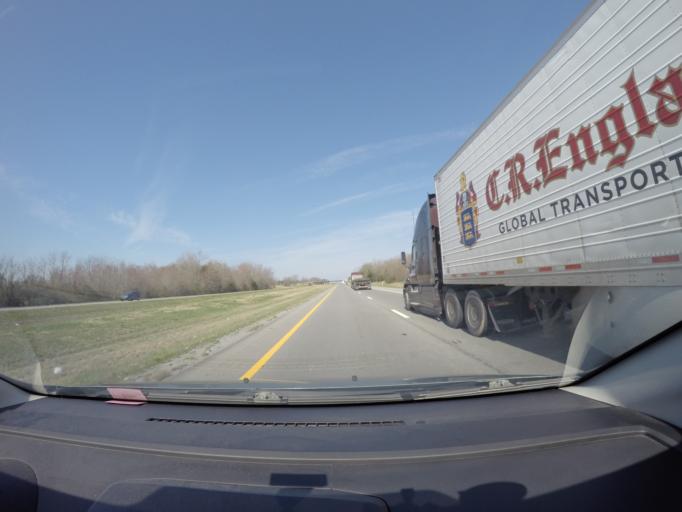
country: US
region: Tennessee
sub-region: Coffee County
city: New Union
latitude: 35.5329
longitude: -86.1567
